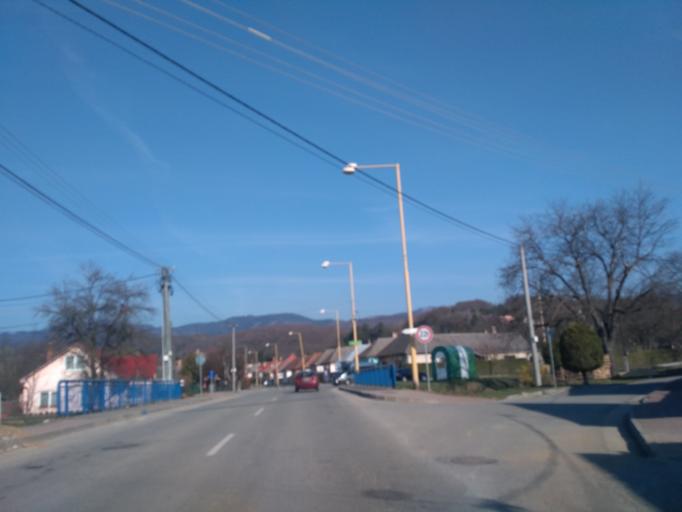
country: SK
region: Kosicky
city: Medzev
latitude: 48.7049
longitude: 20.8854
